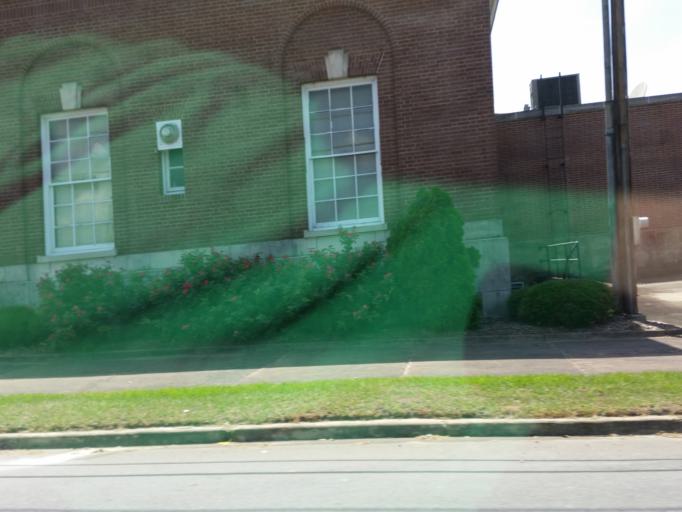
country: US
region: Alabama
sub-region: Marengo County
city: Demopolis
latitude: 32.5187
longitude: -87.8376
